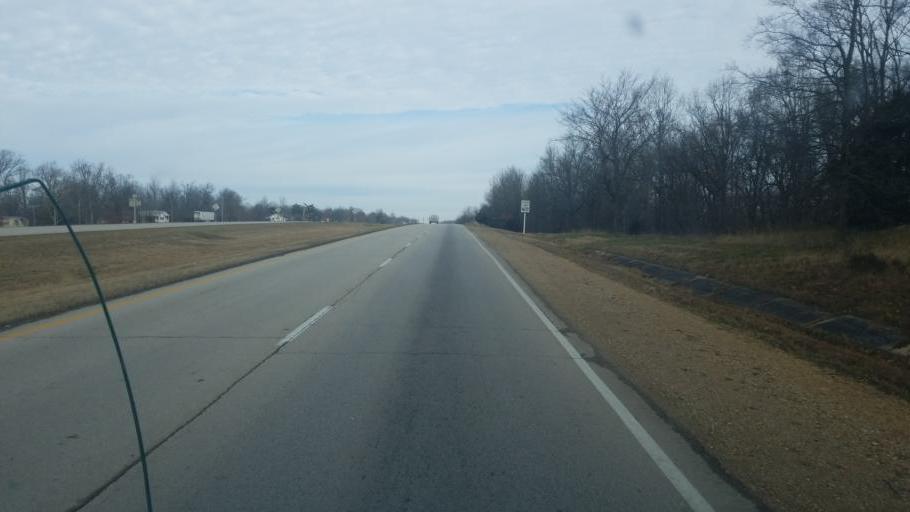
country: US
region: Missouri
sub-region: Stoddard County
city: Dexter
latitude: 36.8197
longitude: -89.9415
